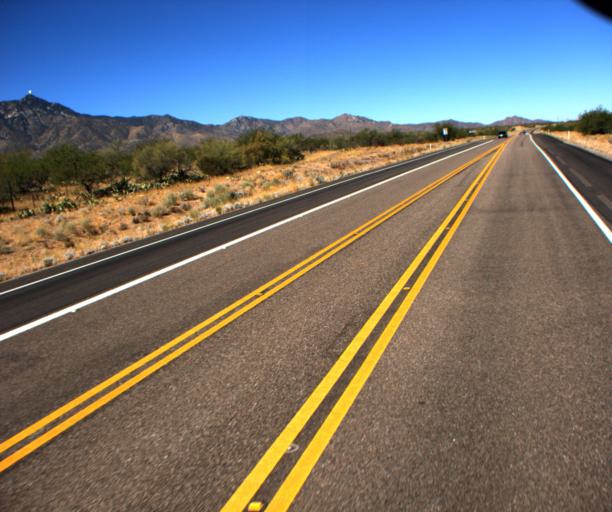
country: US
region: Arizona
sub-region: Pima County
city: Three Points
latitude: 32.0314
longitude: -111.5584
